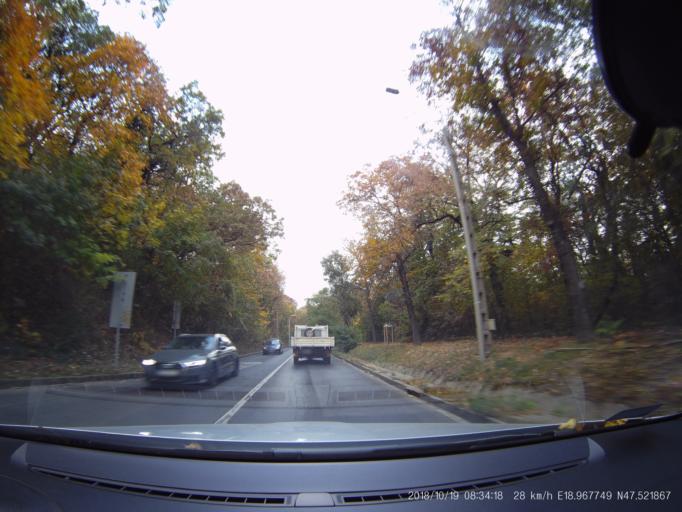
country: HU
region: Pest
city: Budakeszi
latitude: 47.5219
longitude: 18.9677
